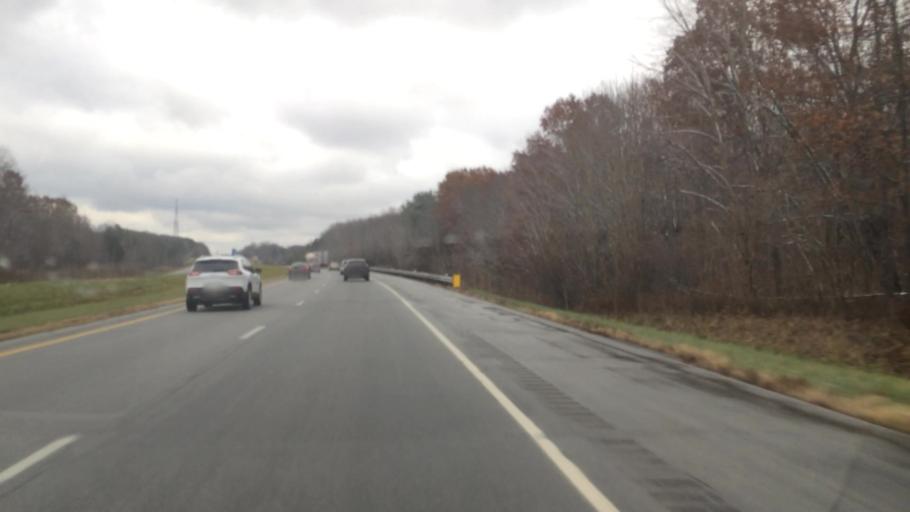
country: US
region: Ohio
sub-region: Summit County
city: Twinsburg
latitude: 41.2820
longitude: -81.4167
